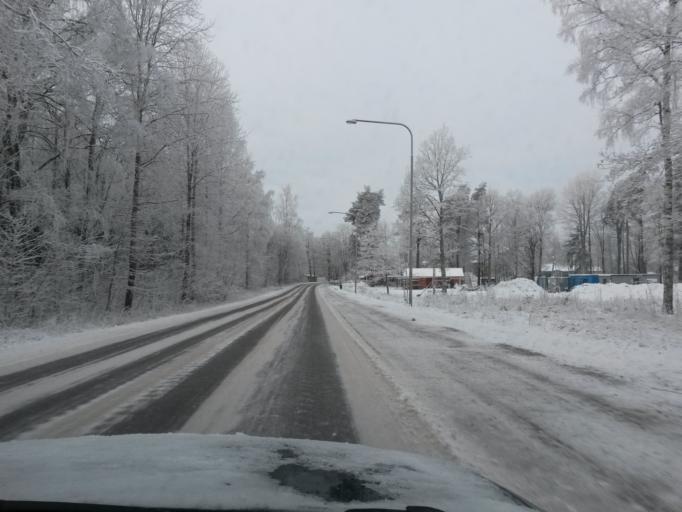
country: SE
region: Vaestra Goetaland
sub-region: Vara Kommun
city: Vara
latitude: 58.3271
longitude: 12.9118
